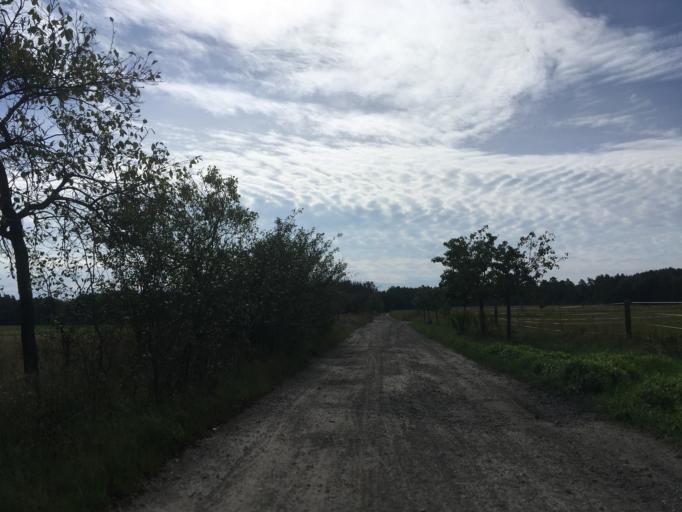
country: DE
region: Brandenburg
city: Birkenwerder
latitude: 52.7570
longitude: 13.3351
